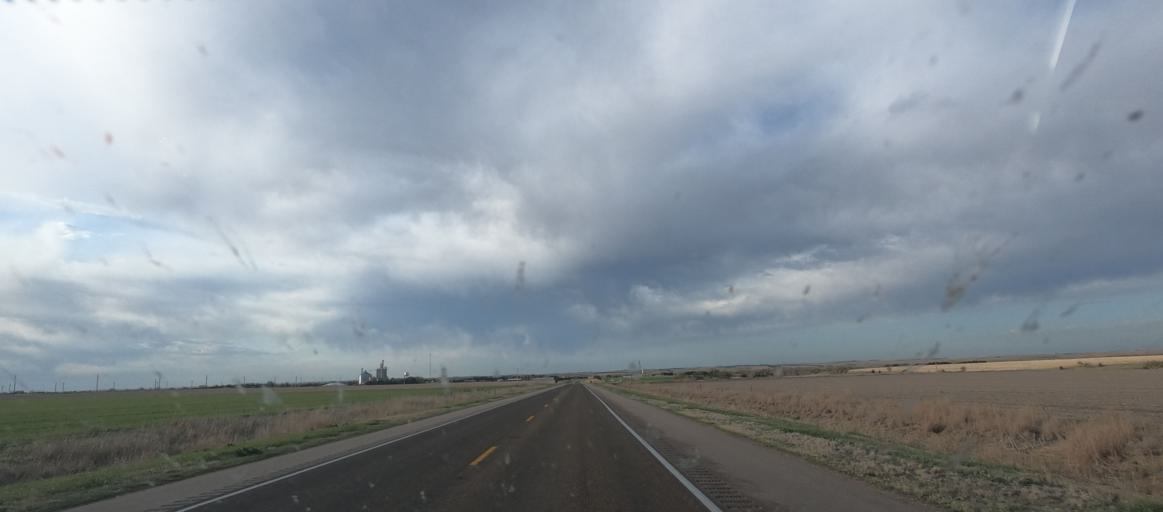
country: US
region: Nebraska
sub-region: Harlan County
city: Alma
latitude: 40.1211
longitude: -99.3677
